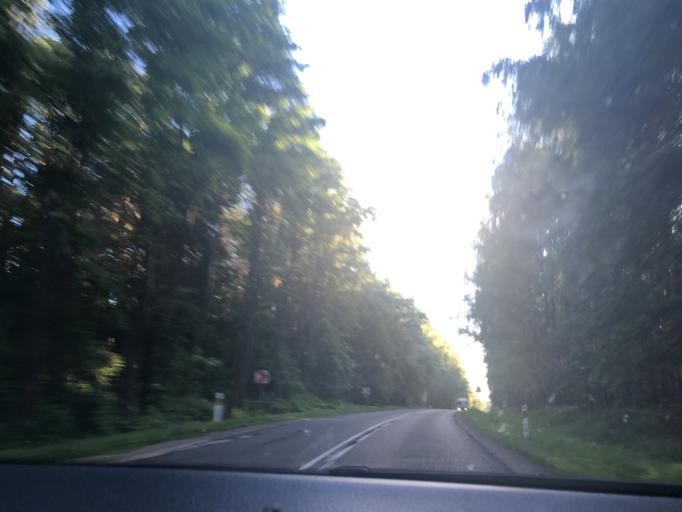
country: PL
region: Masovian Voivodeship
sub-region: Powiat losicki
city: Losice
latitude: 52.2493
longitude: 22.7896
